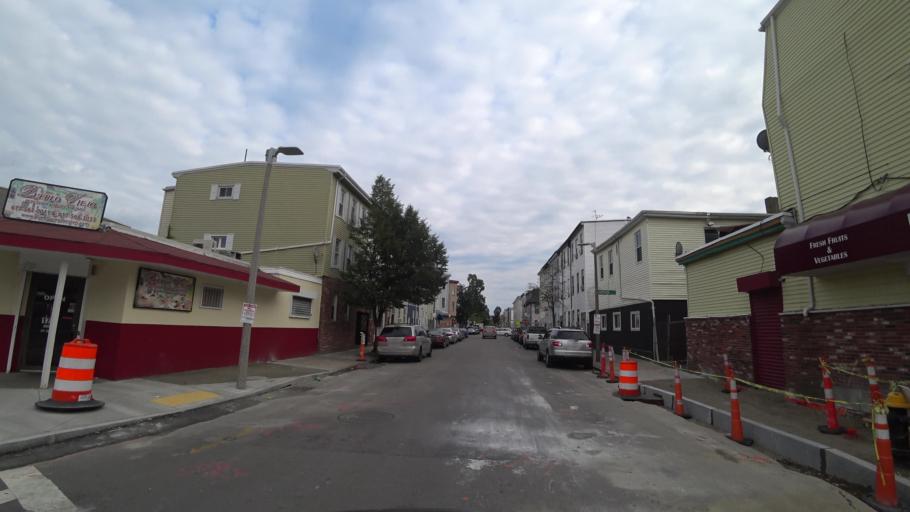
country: US
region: Massachusetts
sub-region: Suffolk County
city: Chelsea
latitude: 42.3760
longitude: -71.0358
